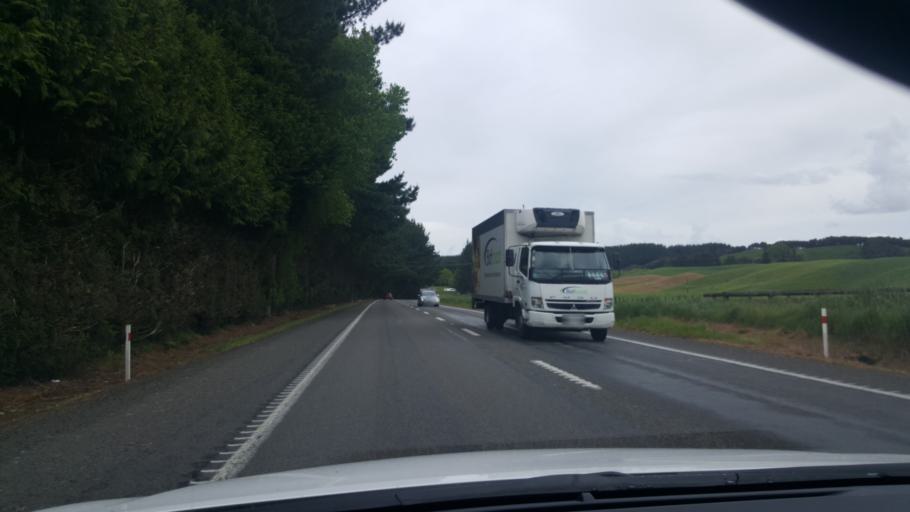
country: NZ
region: Bay of Plenty
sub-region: Rotorua District
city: Rotorua
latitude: -38.2722
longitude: 176.3351
